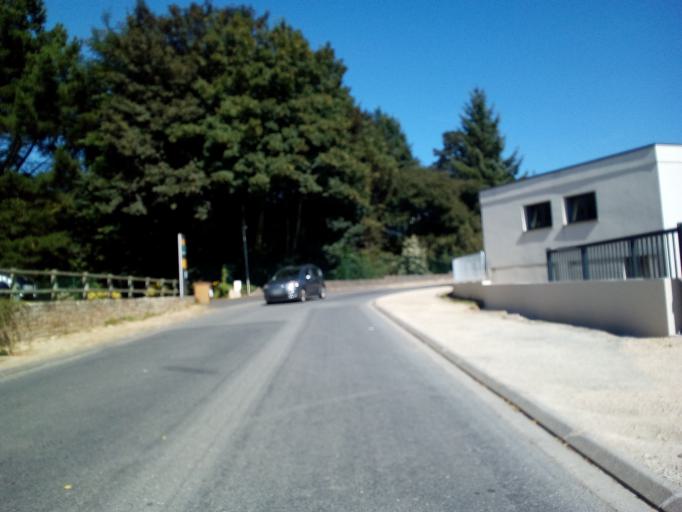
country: FR
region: Brittany
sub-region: Departement du Finistere
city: Landivisiau
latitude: 48.5115
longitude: -4.0682
